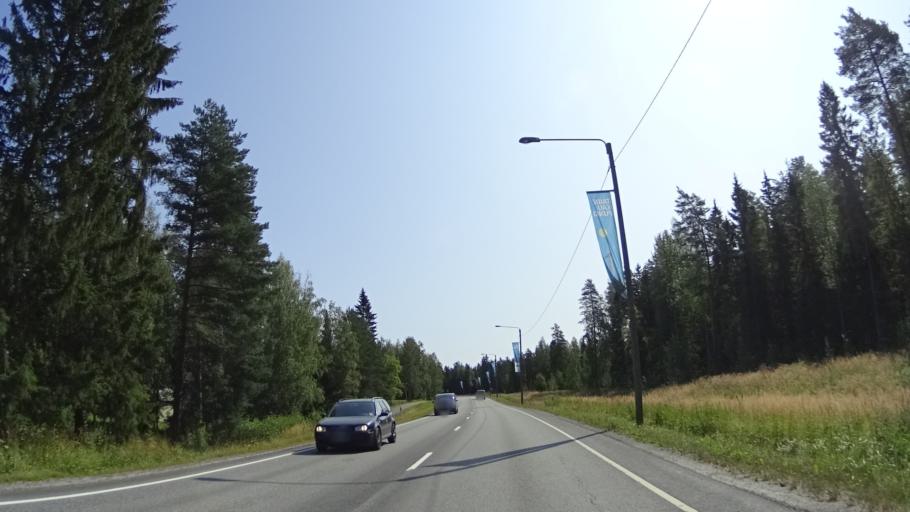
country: FI
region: Pirkanmaa
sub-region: Ylae-Pirkanmaa
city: Maenttae
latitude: 62.0294
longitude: 24.5865
